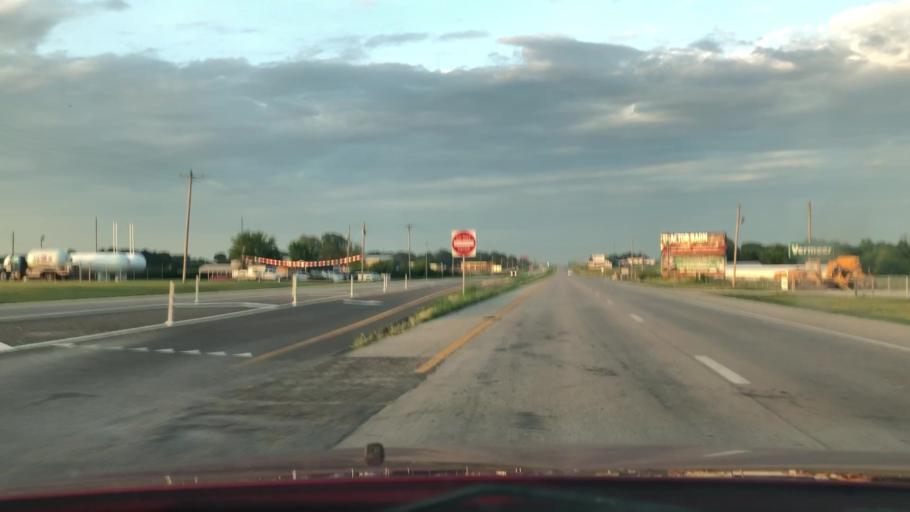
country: US
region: Missouri
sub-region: Greene County
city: Battlefield
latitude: 37.1528
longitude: -93.4154
